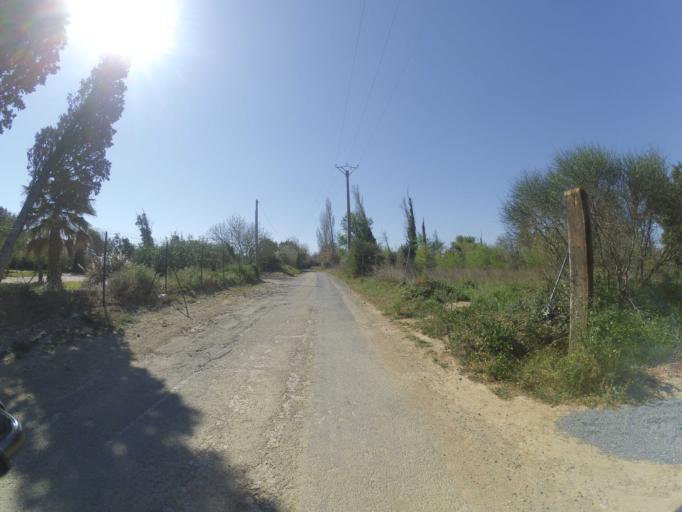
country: FR
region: Languedoc-Roussillon
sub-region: Departement des Pyrenees-Orientales
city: Pezilla-la-Riviere
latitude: 42.7049
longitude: 2.7738
